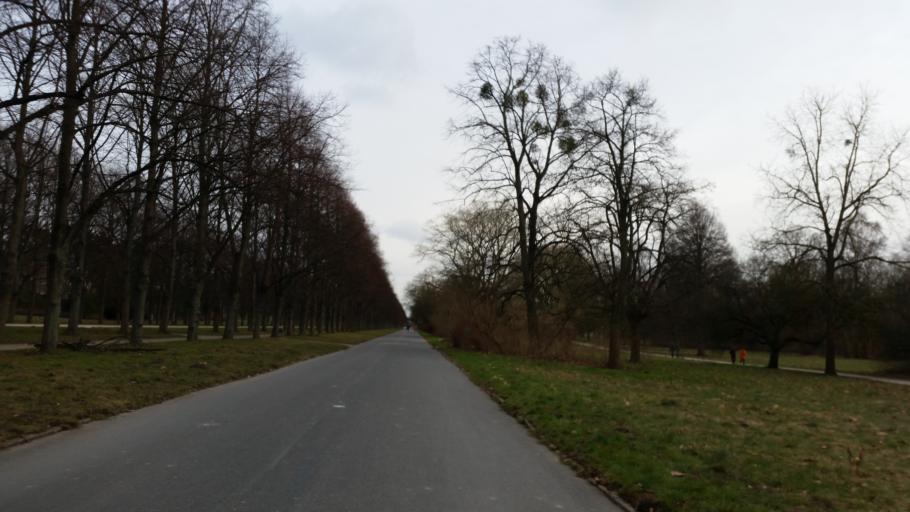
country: DE
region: Lower Saxony
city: Hannover
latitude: 52.3860
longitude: 9.7092
